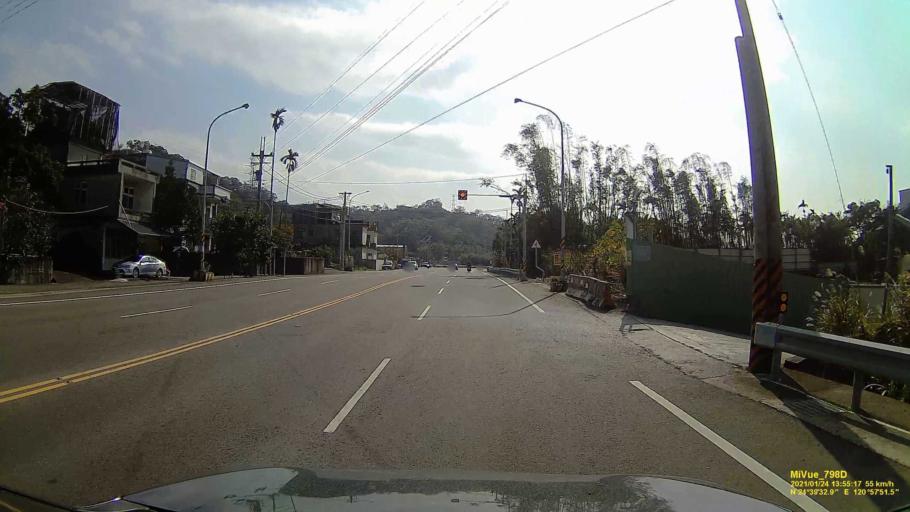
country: TW
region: Taiwan
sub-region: Hsinchu
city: Hsinchu
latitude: 24.6587
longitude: 120.9642
